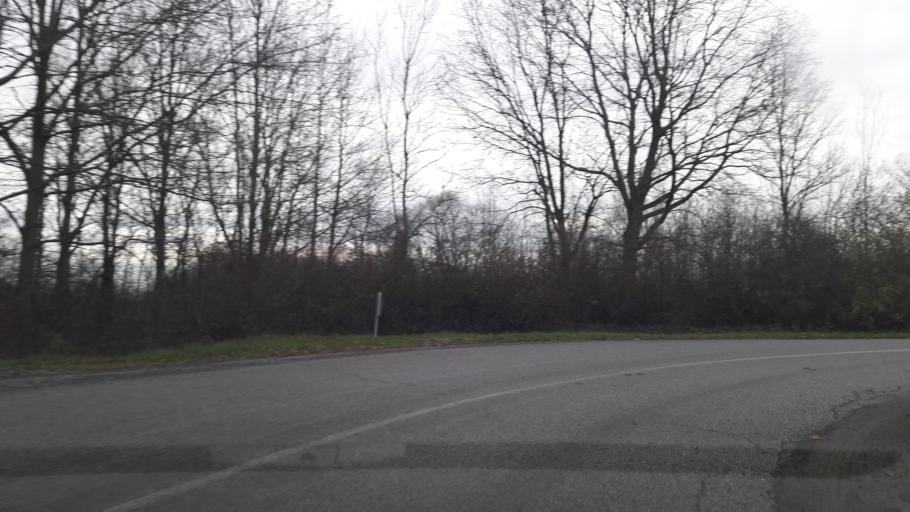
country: HR
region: Osjecko-Baranjska
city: Velimirovac
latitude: 45.6358
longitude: 18.1073
